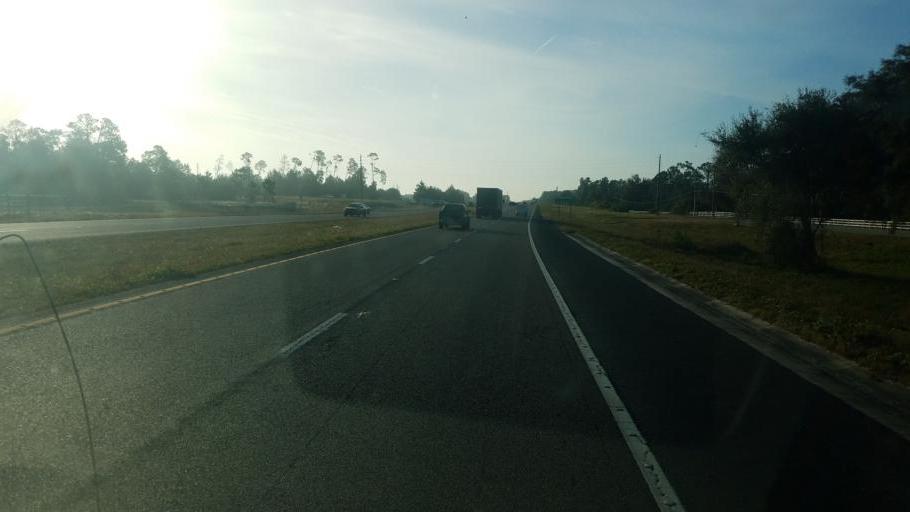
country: US
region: Florida
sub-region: Osceola County
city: Saint Cloud
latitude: 28.2302
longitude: -81.1852
